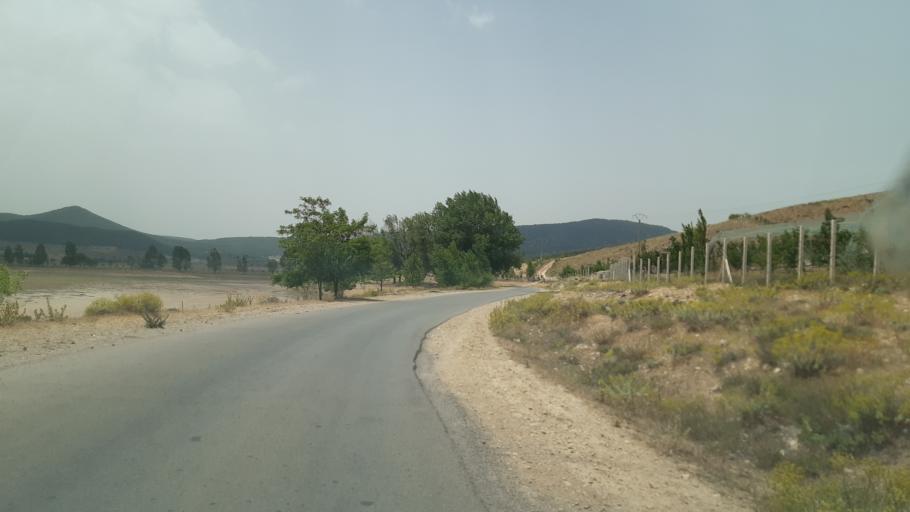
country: MA
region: Meknes-Tafilalet
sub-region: Ifrane
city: Ifrane
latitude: 33.6526
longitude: -5.0153
